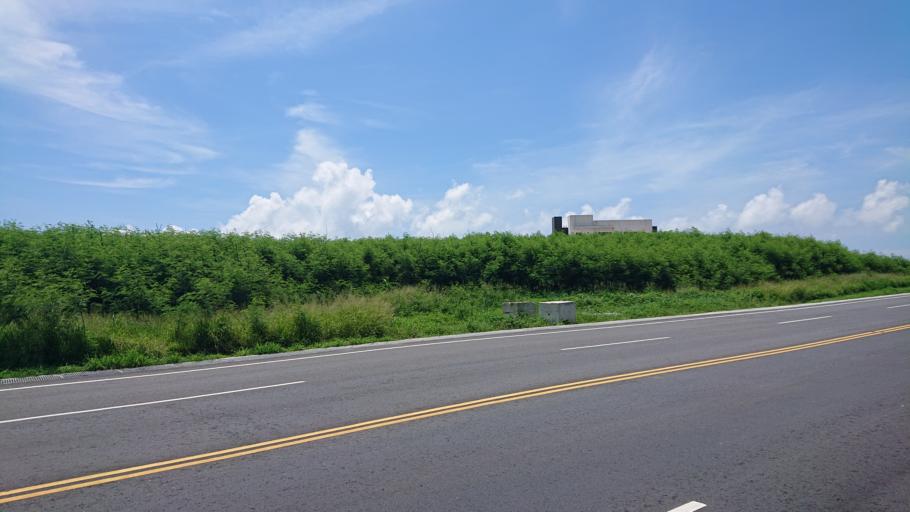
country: TW
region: Taiwan
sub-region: Penghu
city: Ma-kung
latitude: 23.6151
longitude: 119.6076
